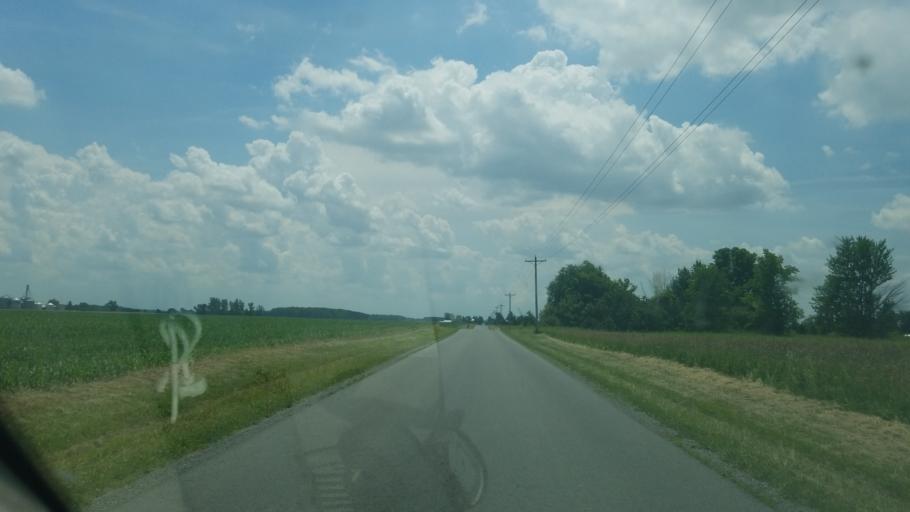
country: US
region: Ohio
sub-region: Hancock County
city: Arlington
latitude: 40.8583
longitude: -83.5998
